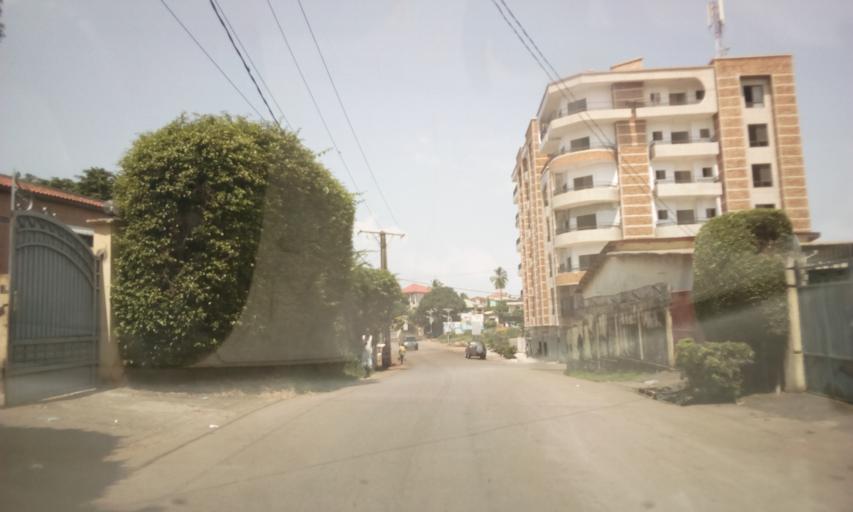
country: GN
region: Conakry
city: Conakry
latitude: 9.5715
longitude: -13.6642
